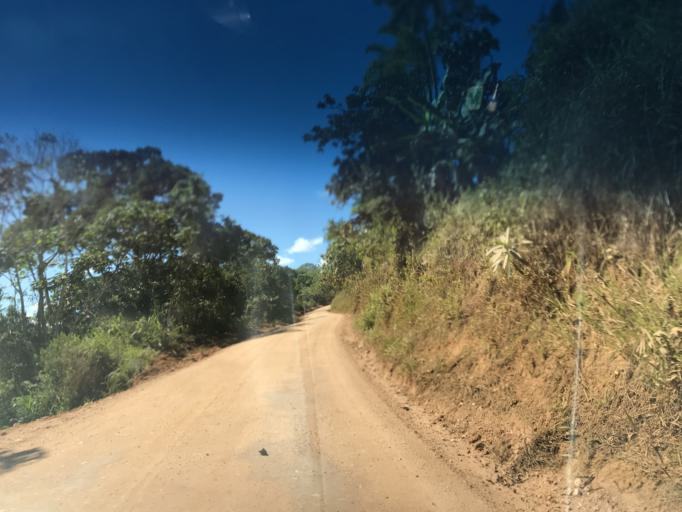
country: BR
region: Bahia
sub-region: Mutuipe
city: Mutuipe
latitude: -13.3730
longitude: -39.3750
